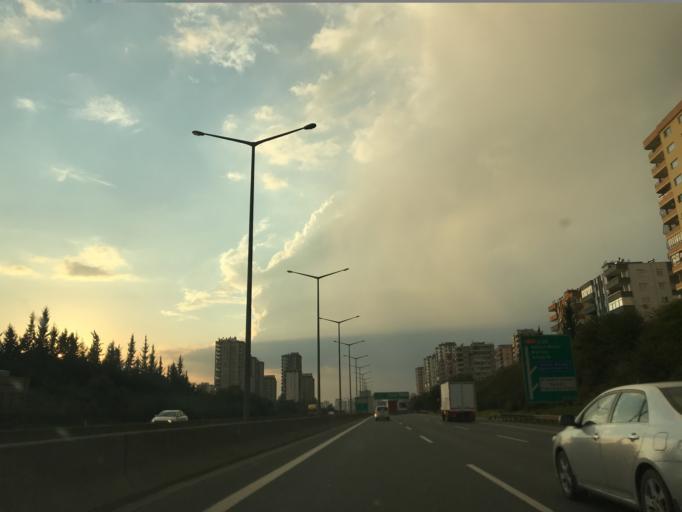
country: TR
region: Adana
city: Seyhan
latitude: 37.0312
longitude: 35.2649
